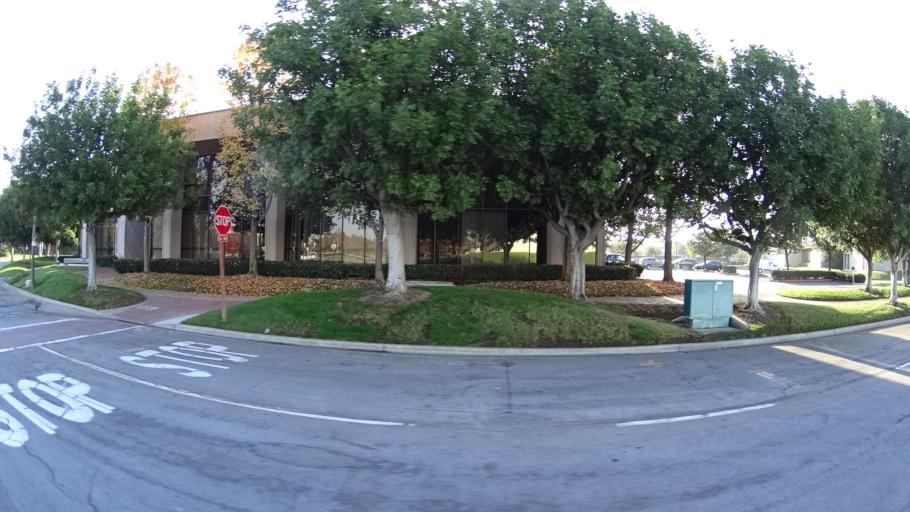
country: US
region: California
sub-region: Orange County
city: Irvine
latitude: 33.6724
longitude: -117.8612
